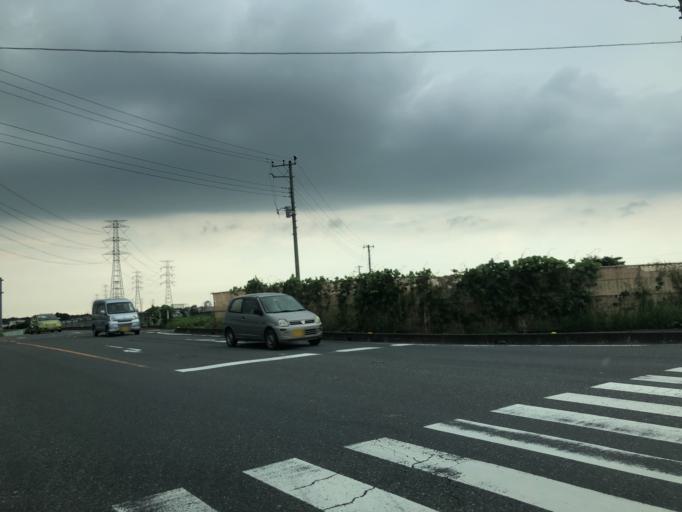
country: JP
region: Saitama
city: Sakado
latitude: 36.0176
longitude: 139.4099
